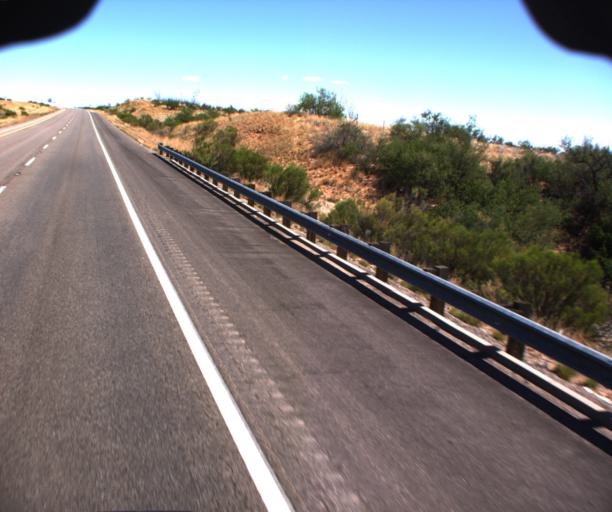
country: US
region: Arizona
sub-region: Cochise County
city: Whetstone
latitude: 31.8406
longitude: -110.3423
